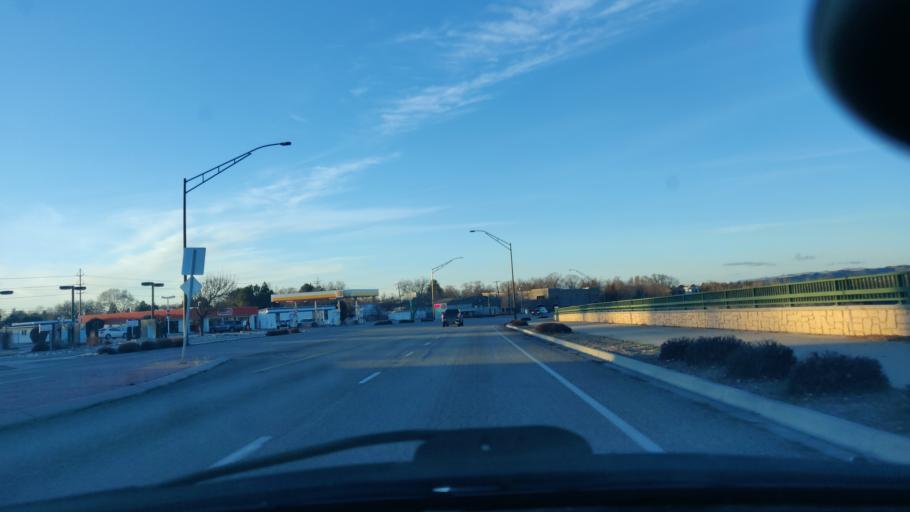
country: US
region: Idaho
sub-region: Ada County
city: Boise
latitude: 43.5778
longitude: -116.1961
